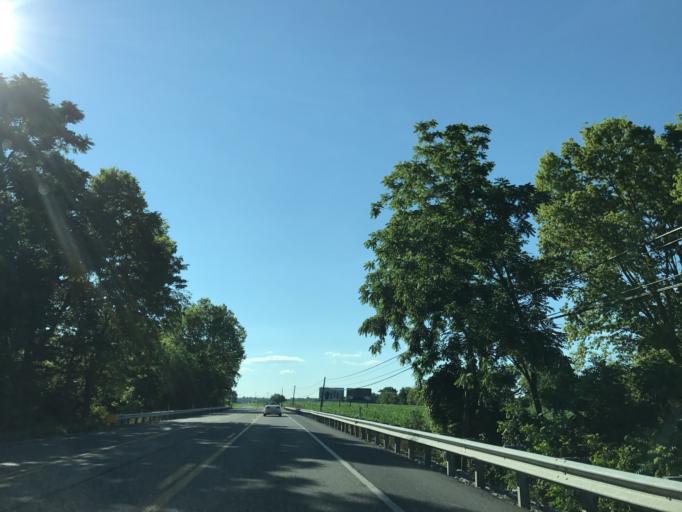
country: US
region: Pennsylvania
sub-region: Lancaster County
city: Rheems
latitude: 40.1242
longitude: -76.5458
